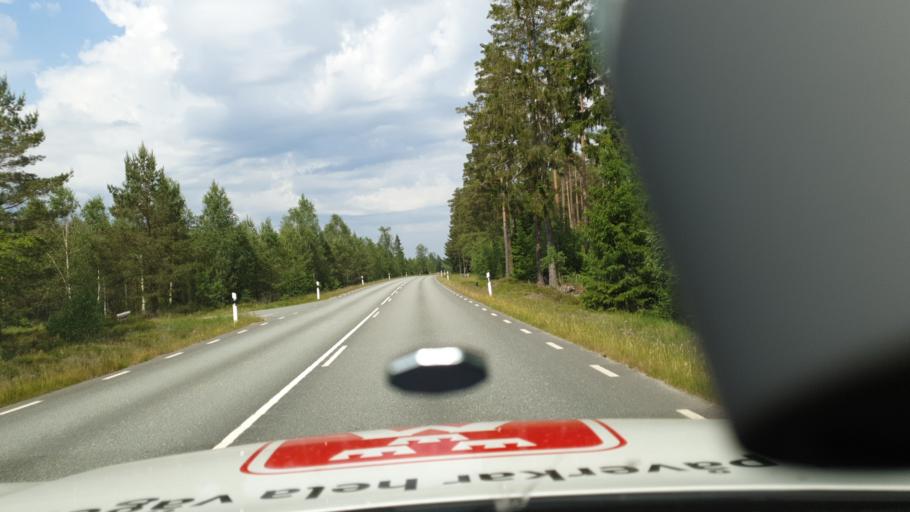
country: SE
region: Joenkoeping
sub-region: Varnamo Kommun
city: Varnamo
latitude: 57.2707
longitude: 14.0554
